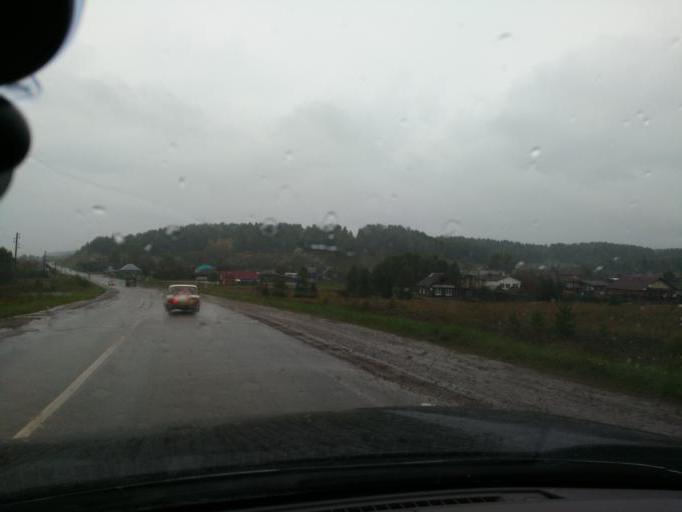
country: RU
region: Perm
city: Osa
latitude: 57.1985
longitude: 55.5920
